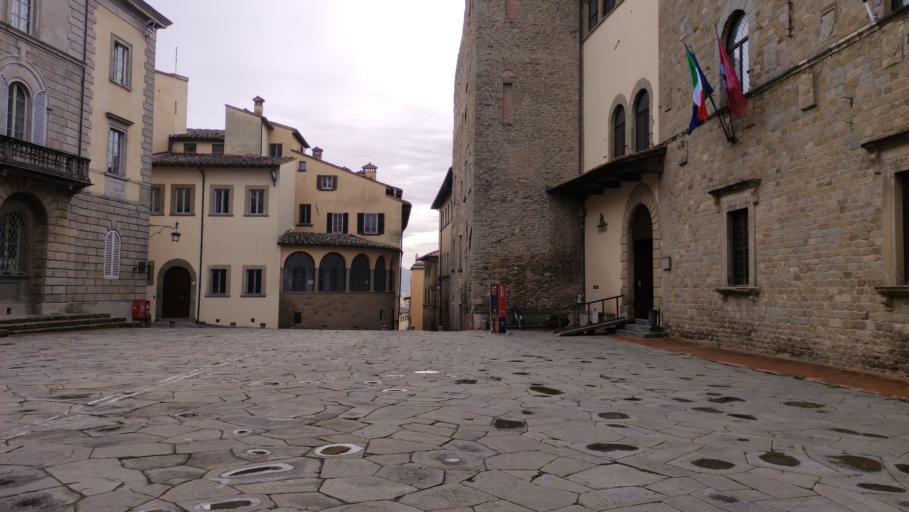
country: IT
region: Tuscany
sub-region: Province of Arezzo
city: Arezzo
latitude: 43.4668
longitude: 11.8826
